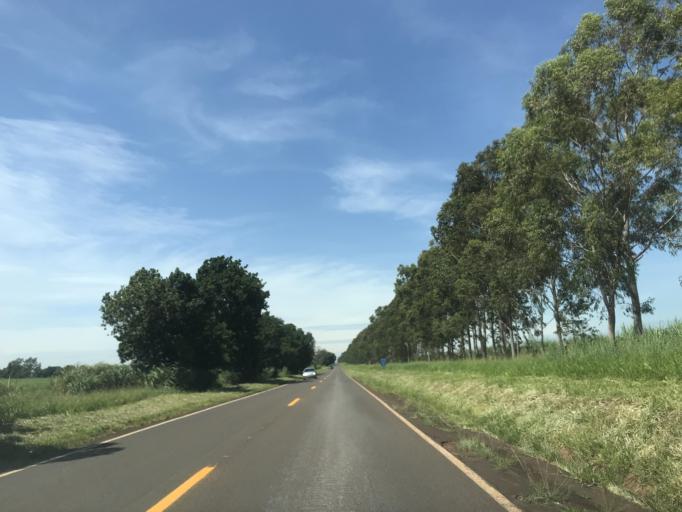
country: BR
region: Parana
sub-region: Paranavai
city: Nova Aurora
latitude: -22.8404
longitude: -52.6568
